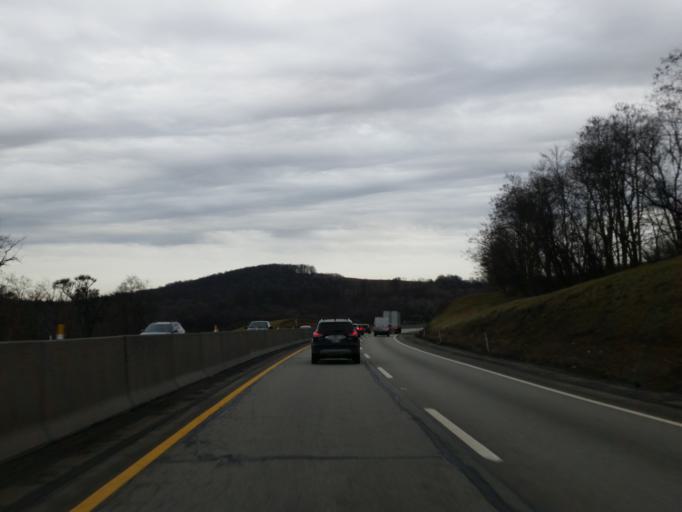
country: US
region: Pennsylvania
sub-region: Somerset County
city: Somerset
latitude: 40.0760
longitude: -79.1659
